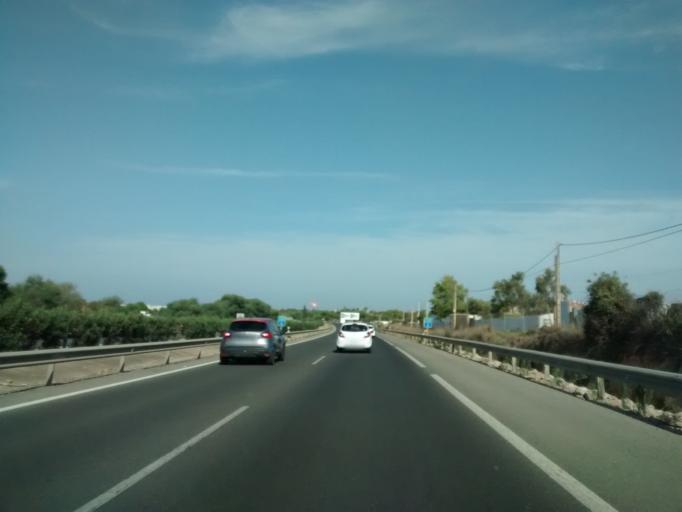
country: ES
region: Andalusia
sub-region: Provincia de Cadiz
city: Chiclana de la Frontera
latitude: 36.4384
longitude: -6.1252
